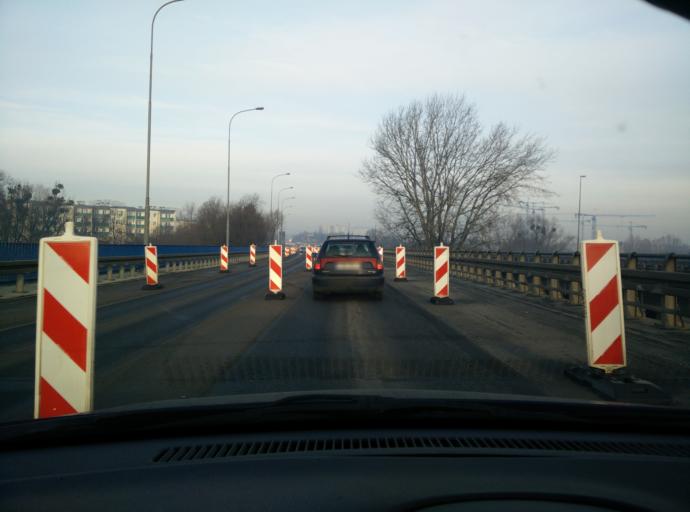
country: PL
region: Greater Poland Voivodeship
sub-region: Poznan
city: Poznan
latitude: 52.3917
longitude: 16.9622
